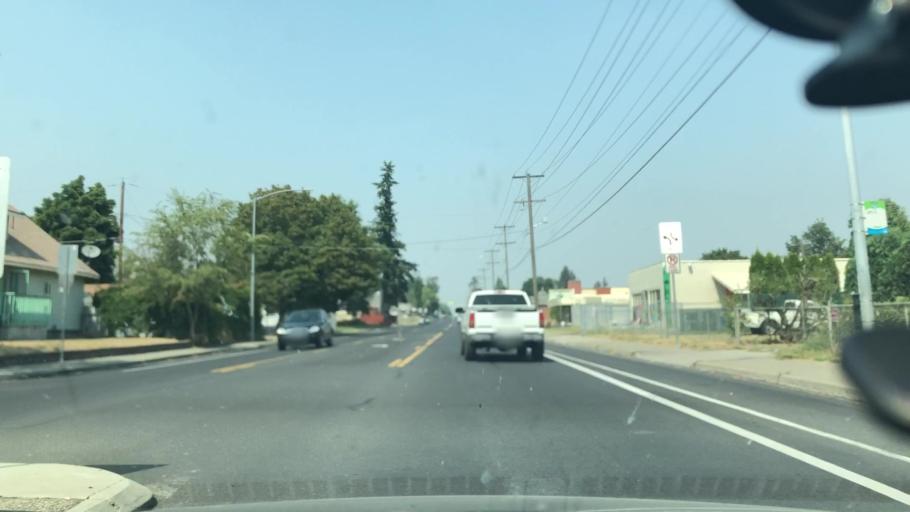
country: US
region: Washington
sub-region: Spokane County
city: Spokane
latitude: 47.6866
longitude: -117.3790
